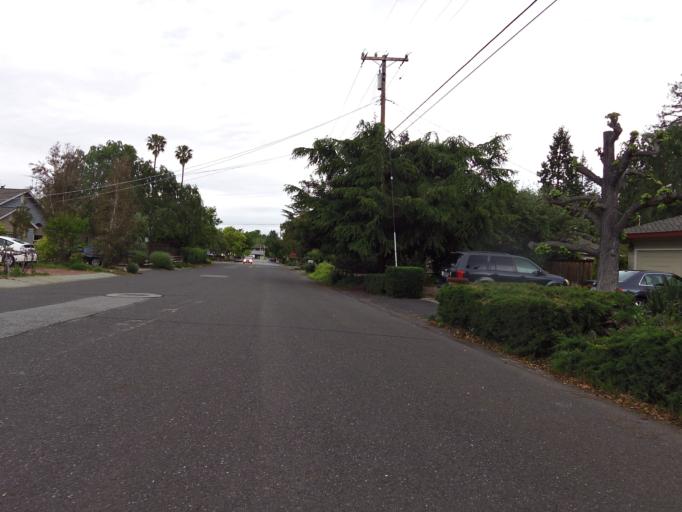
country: US
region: California
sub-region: Santa Clara County
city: Los Altos
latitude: 37.3937
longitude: -122.1051
